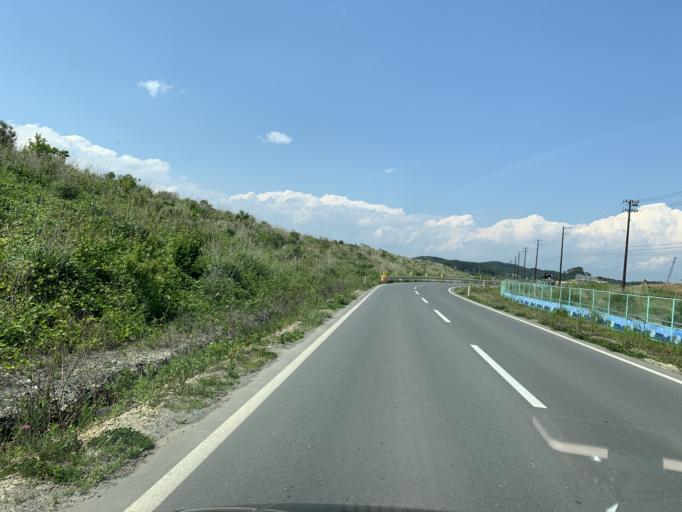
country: JP
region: Miyagi
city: Yamoto
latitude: 38.3599
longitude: 141.1559
